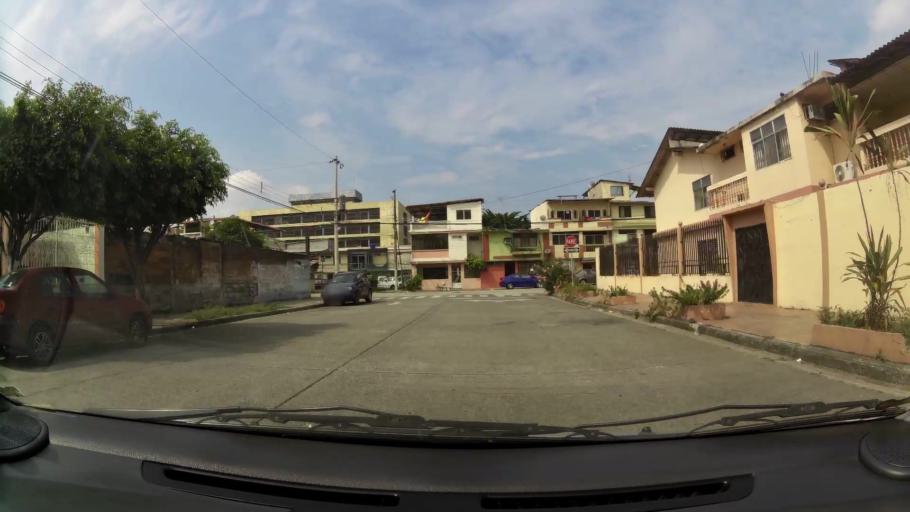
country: EC
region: Guayas
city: Guayaquil
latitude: -2.2427
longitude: -79.8975
